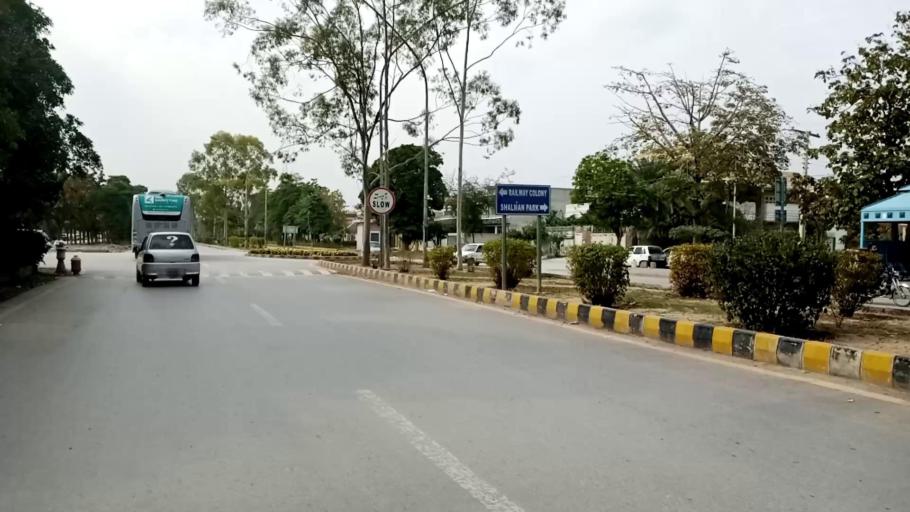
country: PK
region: Khyber Pakhtunkhwa
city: Peshawar
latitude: 33.9564
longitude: 71.4396
